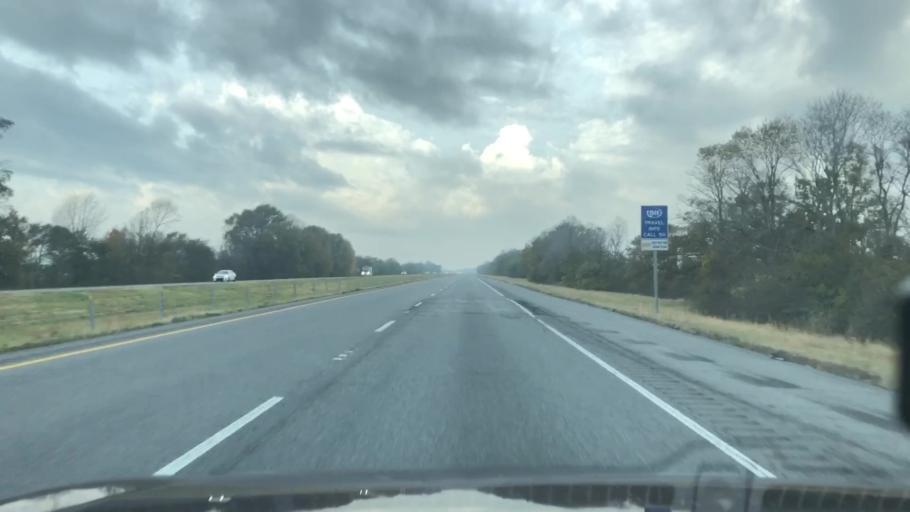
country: US
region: Louisiana
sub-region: Madison Parish
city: Tallulah
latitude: 32.4108
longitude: -91.2542
